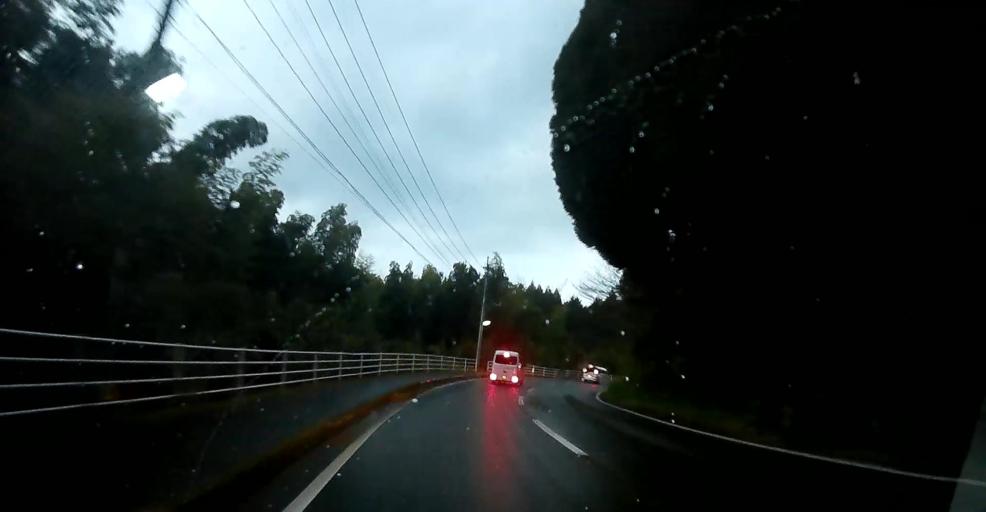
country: JP
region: Kumamoto
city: Ozu
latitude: 32.8365
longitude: 130.9153
